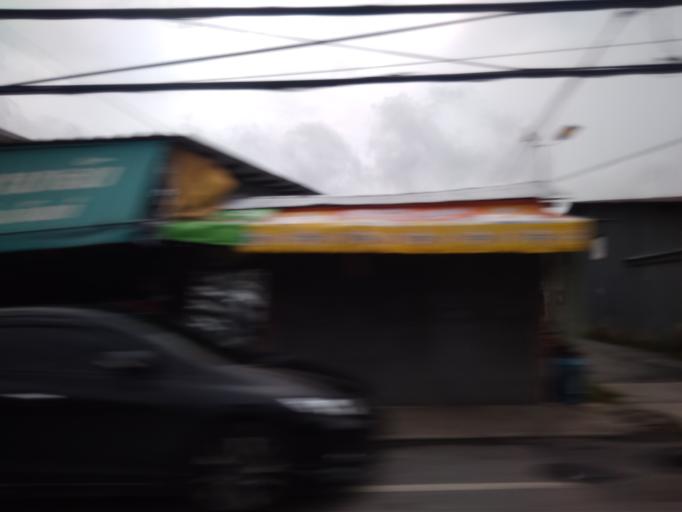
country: TH
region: Phuket
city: Mueang Phuket
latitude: 7.8661
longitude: 98.3805
